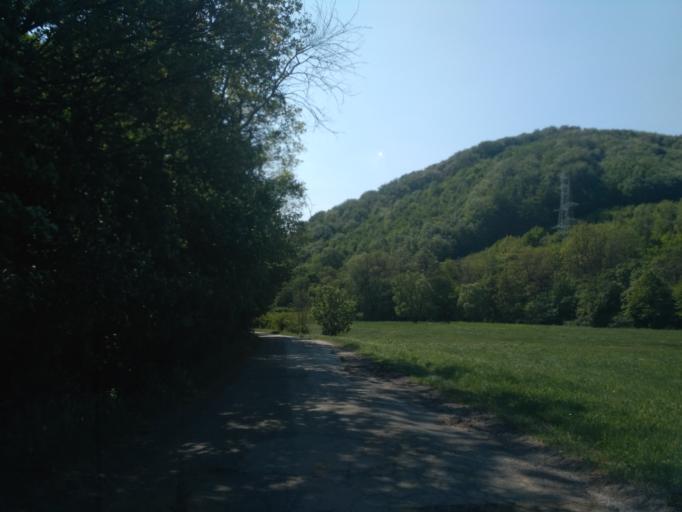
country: SK
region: Kosicky
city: Kosice
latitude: 48.8694
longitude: 21.4151
